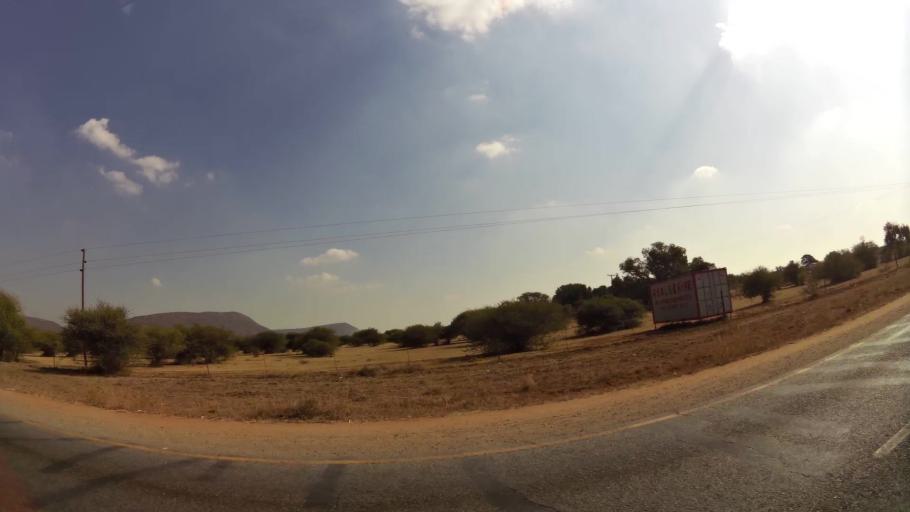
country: ZA
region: North-West
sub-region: Bojanala Platinum District Municipality
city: Mogwase
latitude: -25.4767
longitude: 27.0867
